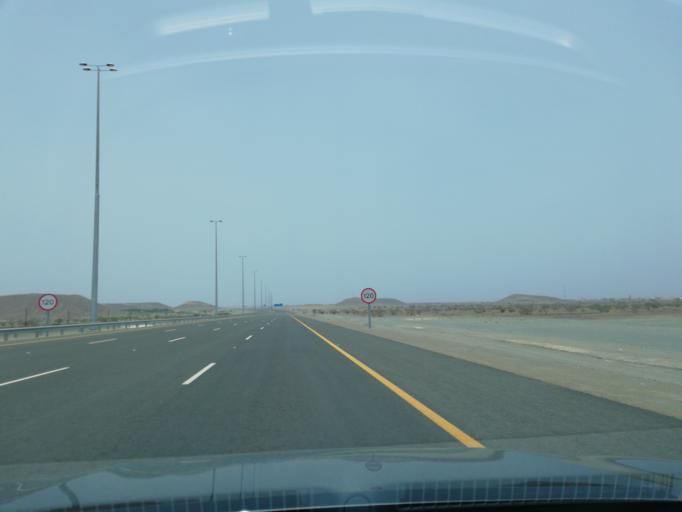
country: OM
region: Al Batinah
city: Al Liwa'
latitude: 24.5069
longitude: 56.5058
